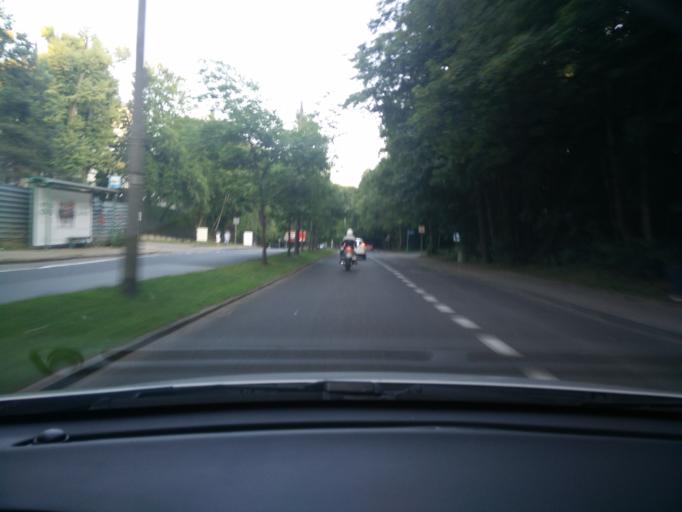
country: PL
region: Pomeranian Voivodeship
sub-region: Sopot
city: Sopot
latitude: 54.4550
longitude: 18.5594
